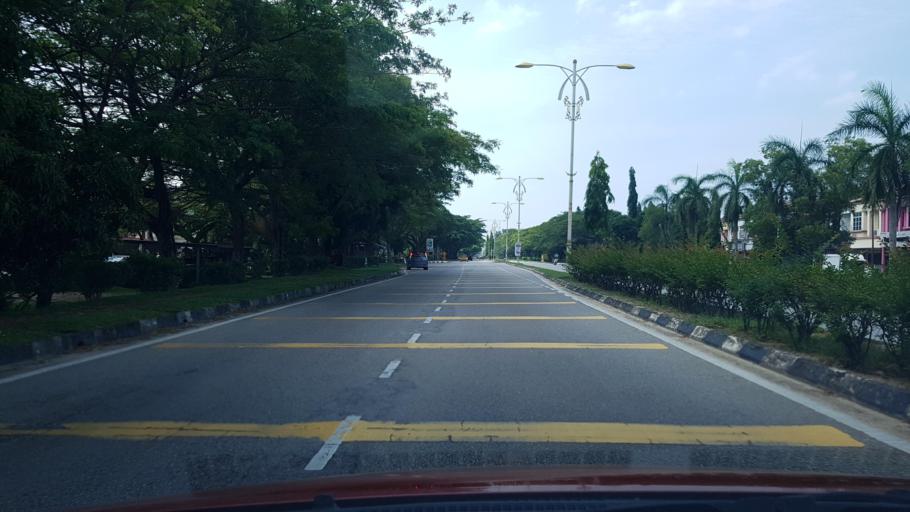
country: MY
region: Terengganu
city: Kuala Terengganu
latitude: 5.3413
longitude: 103.1020
